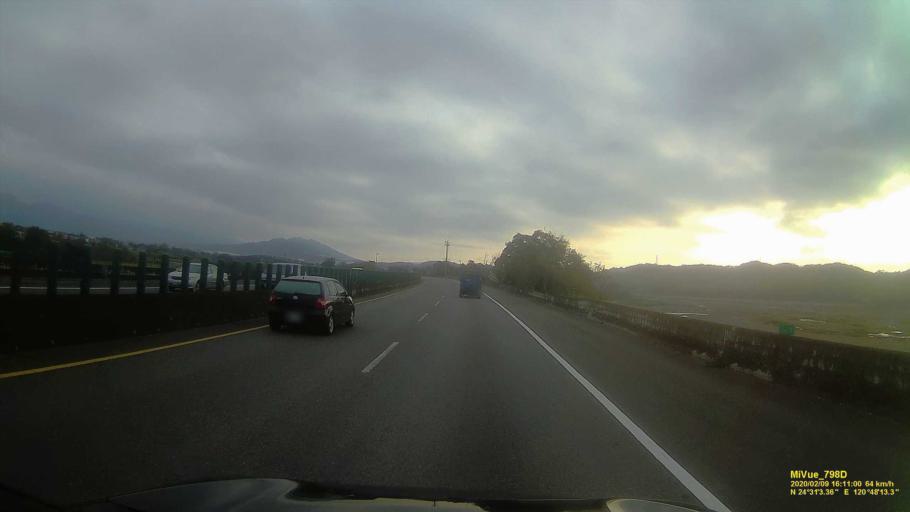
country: TW
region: Taiwan
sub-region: Miaoli
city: Miaoli
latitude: 24.5177
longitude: 120.8038
